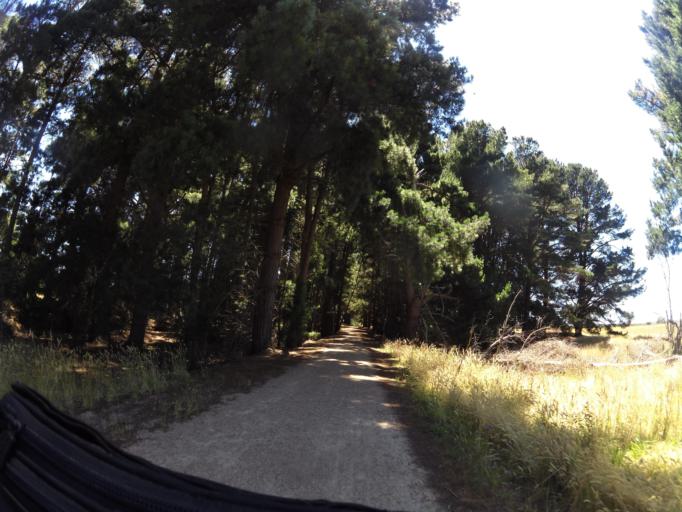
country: AU
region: Victoria
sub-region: Ballarat North
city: Delacombe
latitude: -37.6621
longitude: 143.6631
